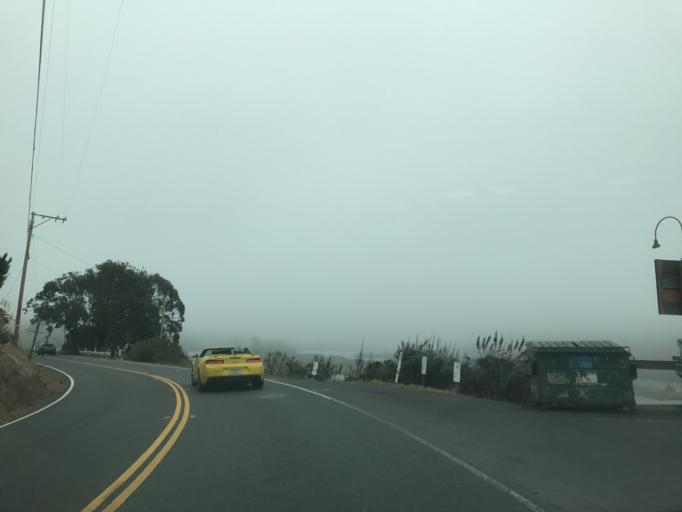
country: US
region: California
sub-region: Sonoma County
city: Monte Rio
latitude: 38.4506
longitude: -123.1246
